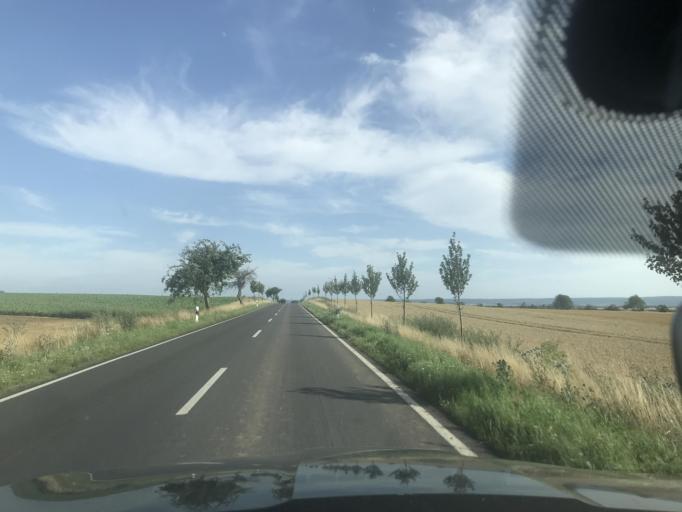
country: DE
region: Saxony-Anhalt
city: Ditfurt
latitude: 51.8522
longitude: 11.1903
